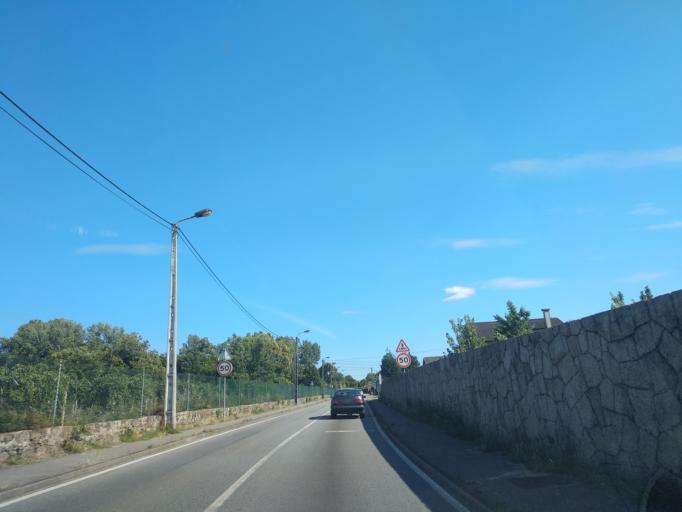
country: PT
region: Braga
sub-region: Vila Verde
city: Prado
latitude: 41.5910
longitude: -8.4591
